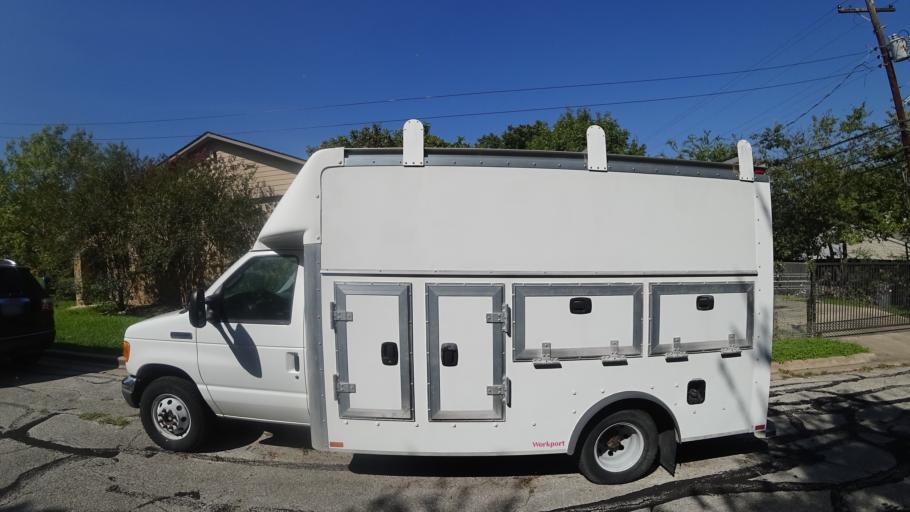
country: US
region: Texas
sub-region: Travis County
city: Austin
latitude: 30.3201
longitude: -97.6807
